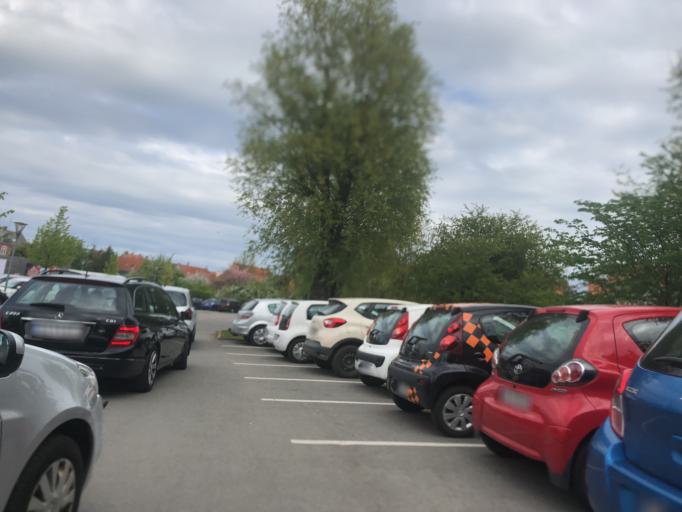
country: DK
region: Zealand
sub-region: Koge Kommune
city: Koge
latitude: 55.4559
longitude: 12.1770
